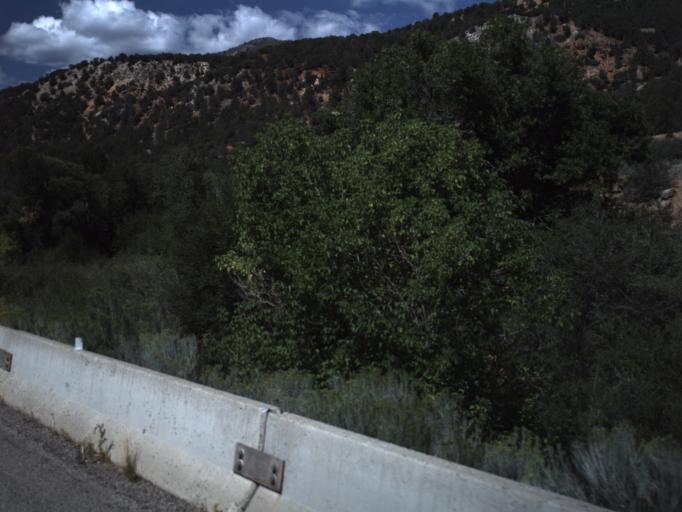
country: US
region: Utah
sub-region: Utah County
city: Woodland Hills
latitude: 39.9617
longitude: -111.5232
